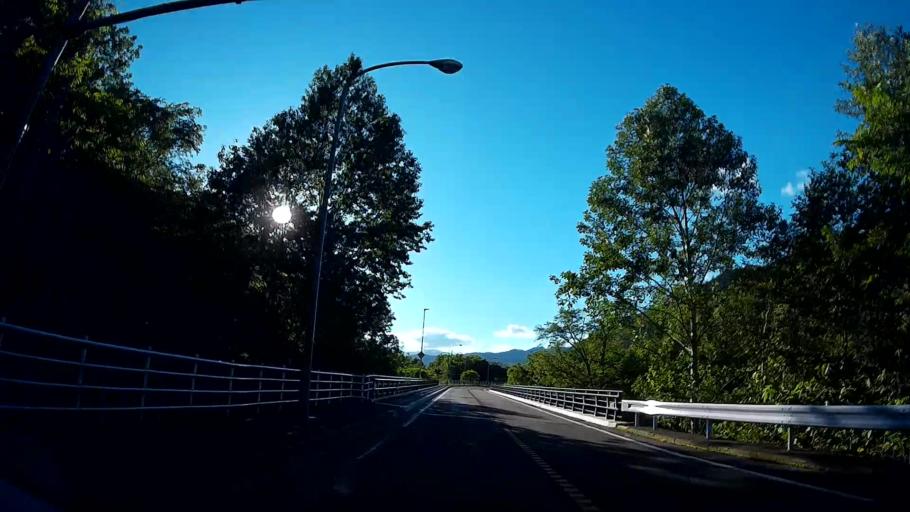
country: JP
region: Hokkaido
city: Sapporo
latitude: 42.9768
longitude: 141.1372
